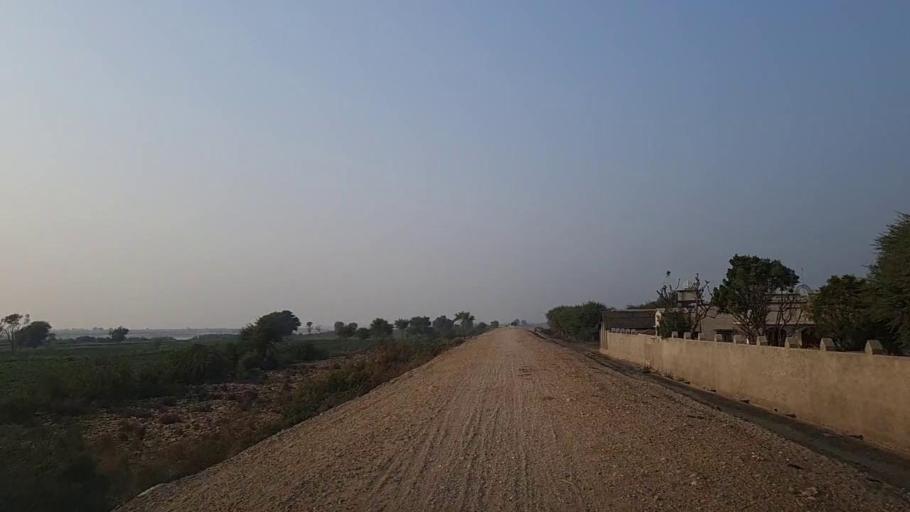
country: PK
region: Sindh
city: Sann
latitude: 26.1241
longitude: 68.1427
